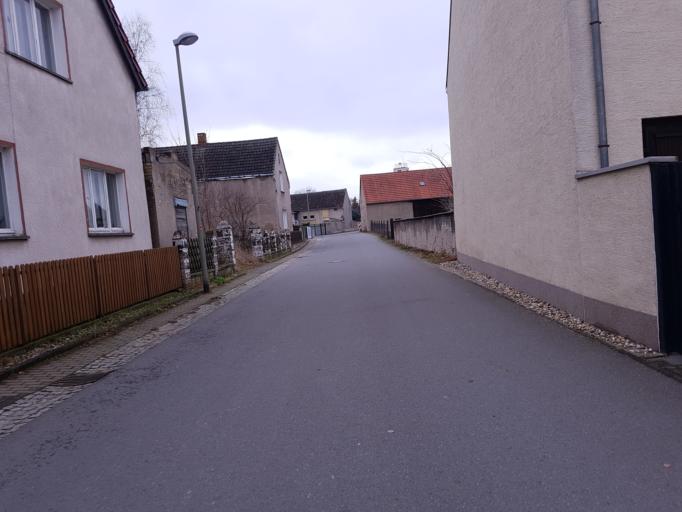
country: DE
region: Brandenburg
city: Groden
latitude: 51.4063
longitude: 13.5724
